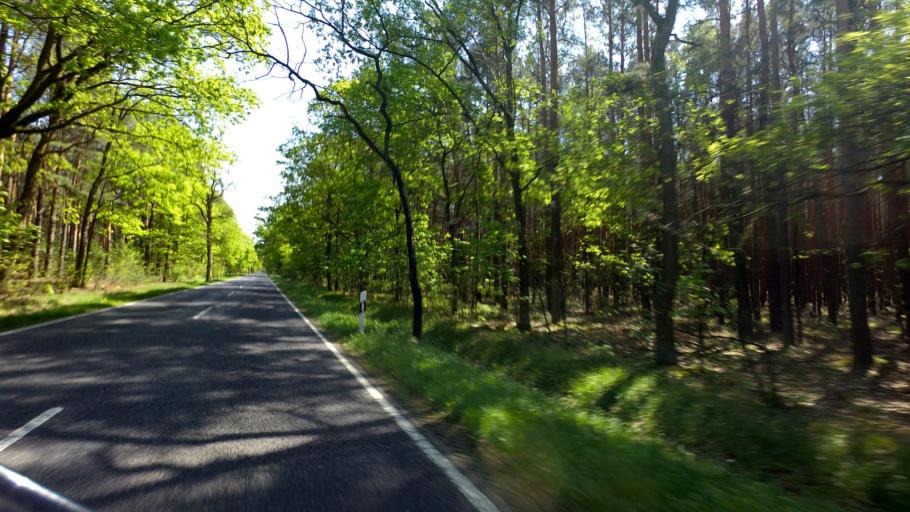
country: DE
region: Brandenburg
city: Munchehofe
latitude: 52.0999
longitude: 13.8220
